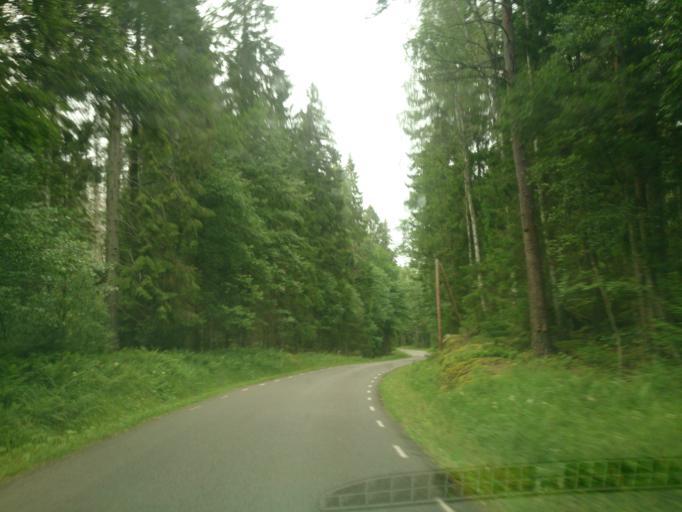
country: SE
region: OEstergoetland
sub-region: Atvidabergs Kommun
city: Atvidaberg
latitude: 58.2883
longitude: 16.0950
